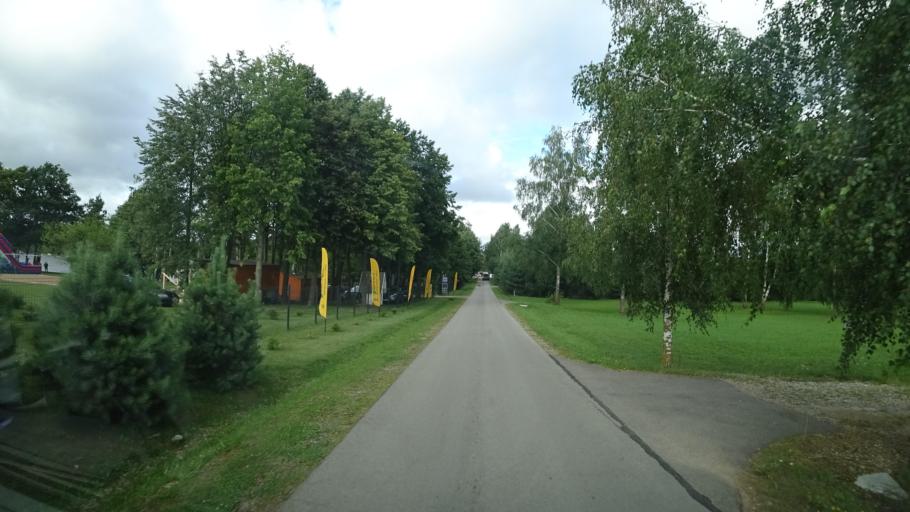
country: LT
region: Marijampoles apskritis
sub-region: Marijampole Municipality
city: Marijampole
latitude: 54.5194
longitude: 23.3388
